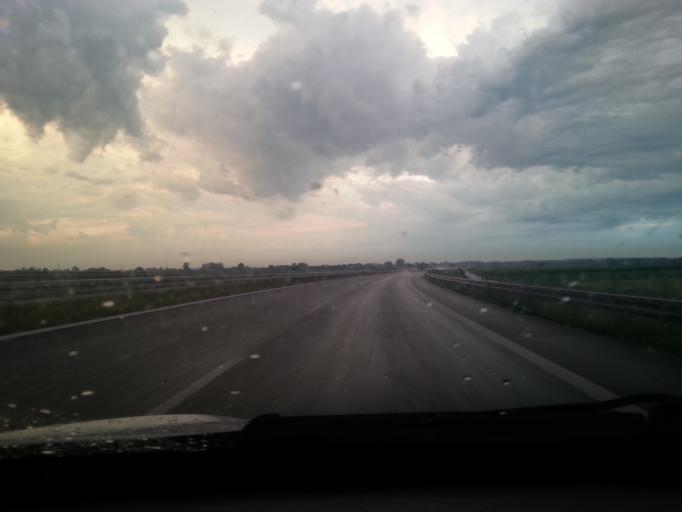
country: PL
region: Lodz Voivodeship
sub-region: Powiat pabianicki
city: Ksawerow
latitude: 51.6954
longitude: 19.3915
